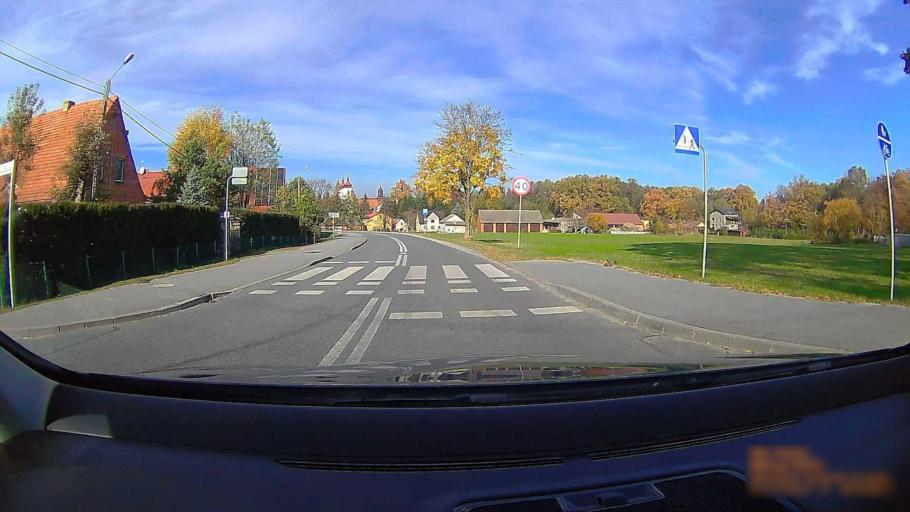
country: PL
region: Greater Poland Voivodeship
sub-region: Powiat ostrzeszowski
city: Doruchow
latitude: 51.3593
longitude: 18.0305
